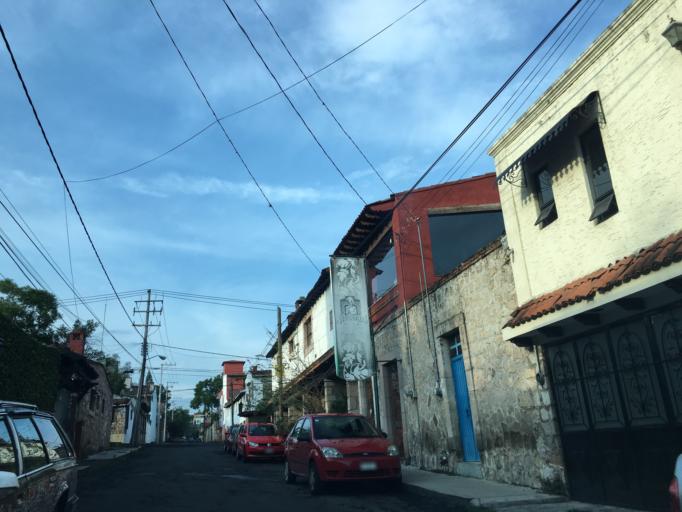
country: MX
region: Michoacan
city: Morelia
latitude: 19.6795
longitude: -101.1957
